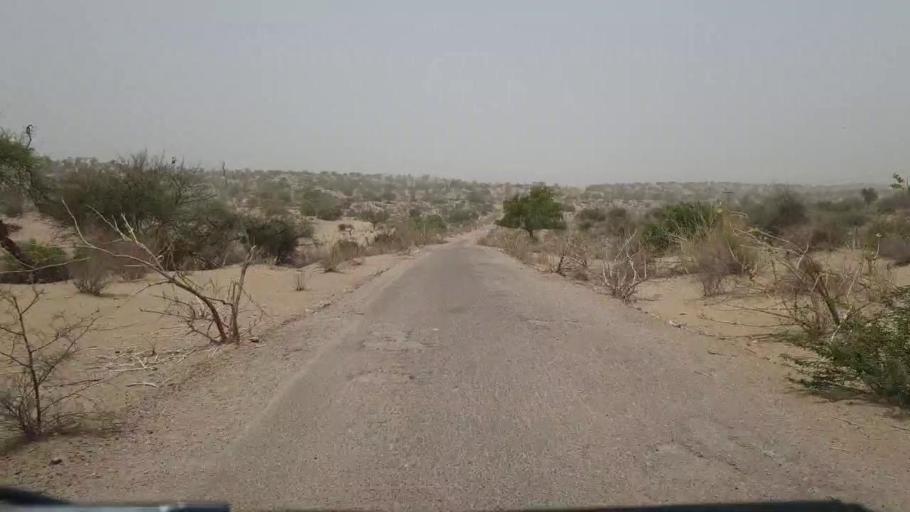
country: PK
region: Sindh
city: Naukot
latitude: 24.7401
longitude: 69.5477
